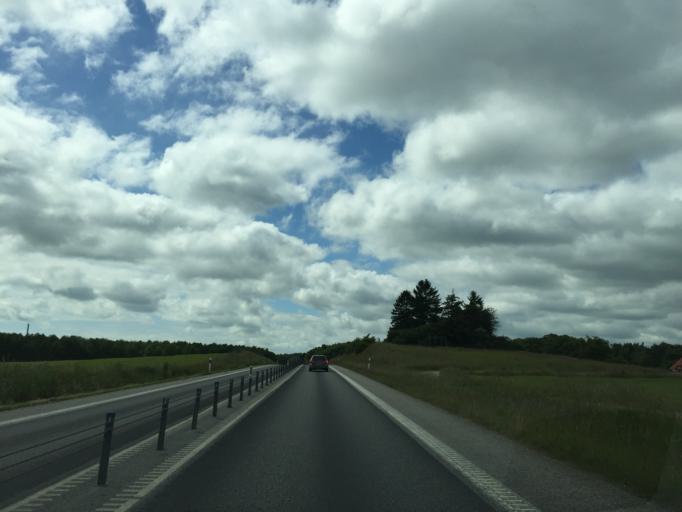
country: SE
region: Skane
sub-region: Trelleborgs Kommun
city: Anderslov
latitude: 55.5066
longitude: 13.3403
